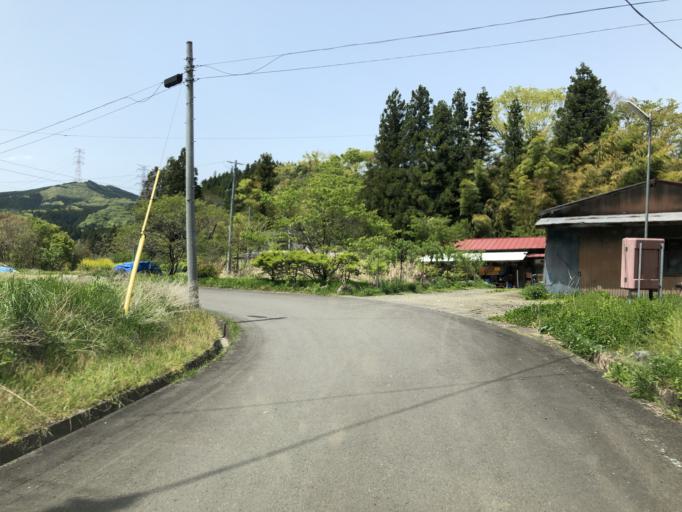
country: JP
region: Fukushima
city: Ishikawa
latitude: 37.0126
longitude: 140.3486
